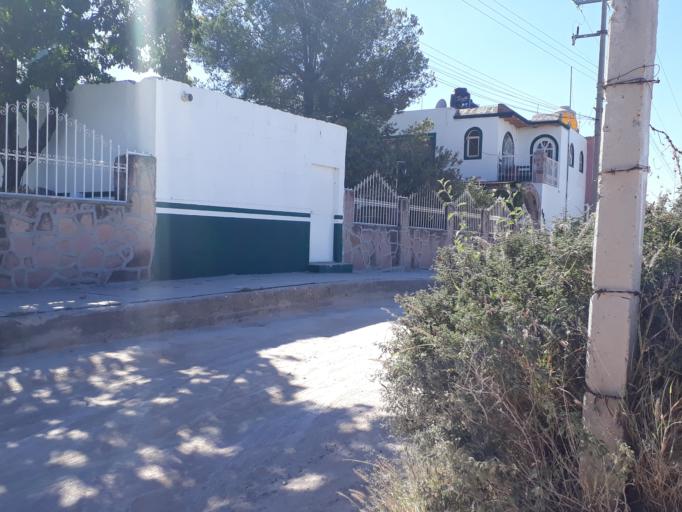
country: MX
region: Aguascalientes
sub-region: Aguascalientes
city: Villa Licenciado Jesus Teran (Calvillito)
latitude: 21.8607
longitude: -102.2302
